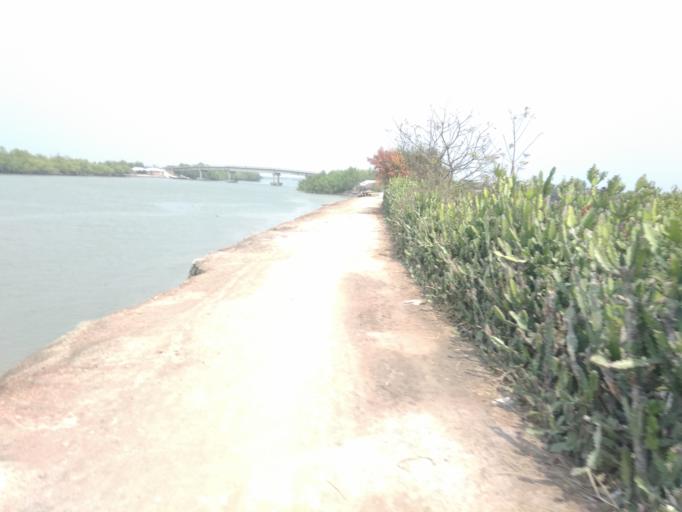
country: IN
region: West Bengal
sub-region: North 24 Parganas
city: Taki
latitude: 22.2864
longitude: 89.2719
